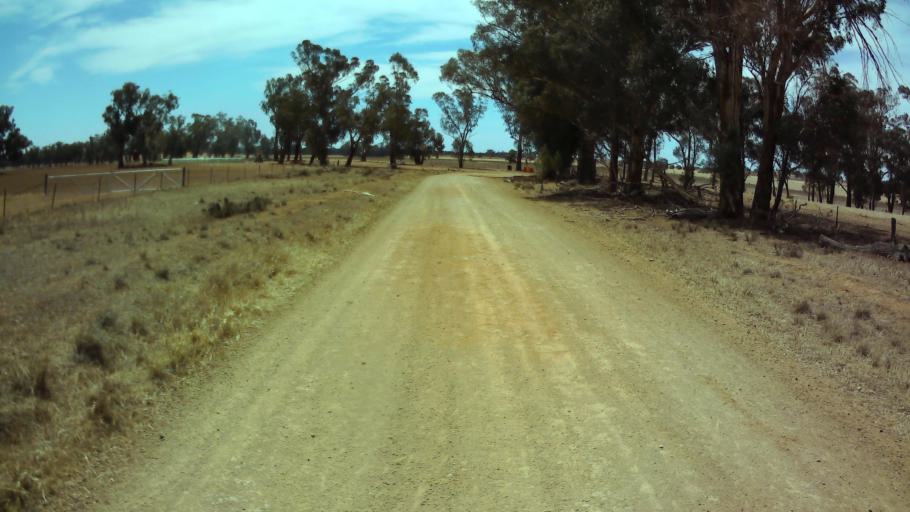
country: AU
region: New South Wales
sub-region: Weddin
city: Grenfell
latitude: -33.7594
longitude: 148.1403
